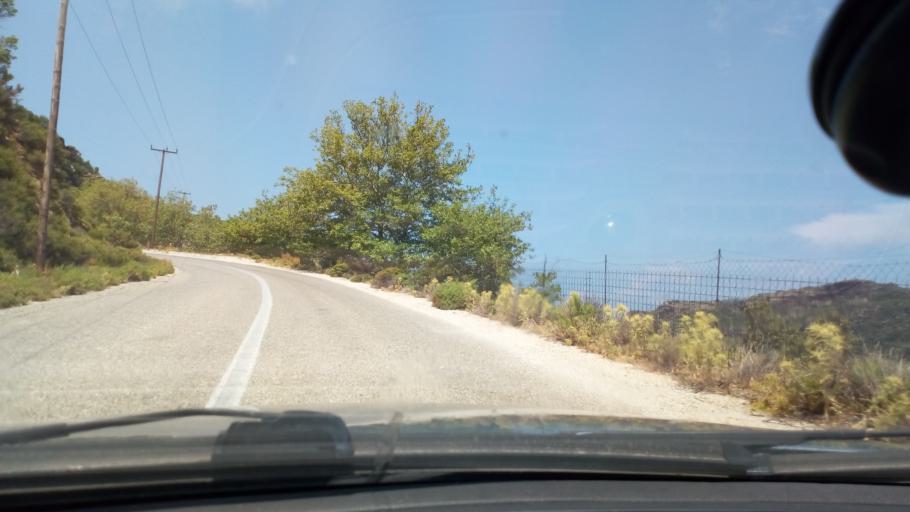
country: GR
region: North Aegean
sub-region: Nomos Samou
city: Agios Kirykos
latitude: 37.6367
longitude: 26.2575
